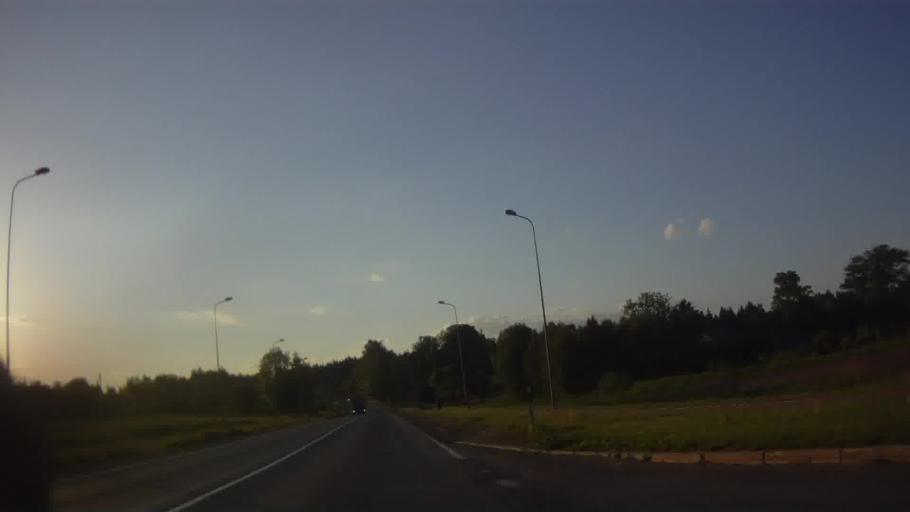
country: LV
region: Jekabpils Rajons
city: Jekabpils
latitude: 56.5400
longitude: 25.8146
